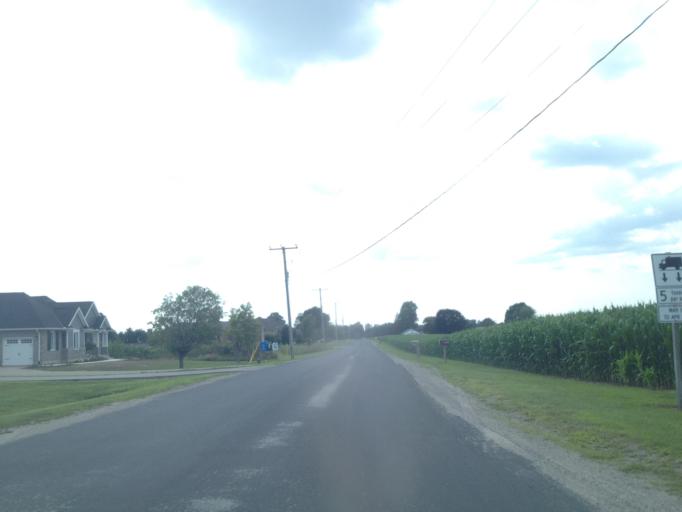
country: CA
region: Ontario
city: Aylmer
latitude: 42.6808
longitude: -80.9855
